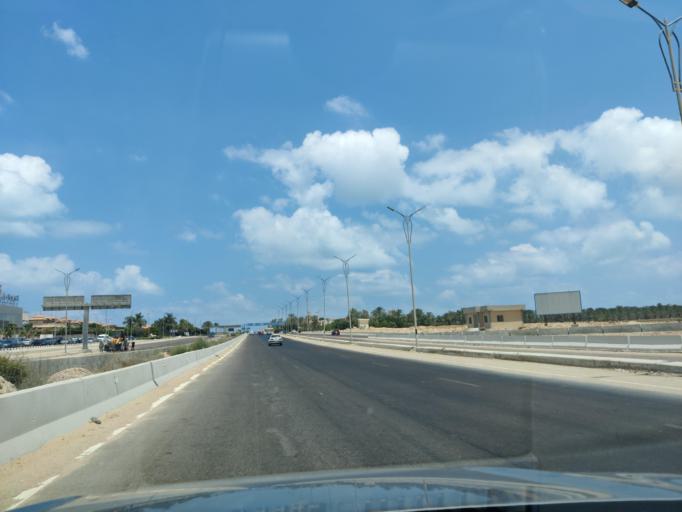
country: EG
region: Alexandria
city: Alexandria
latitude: 31.0055
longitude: 29.6400
